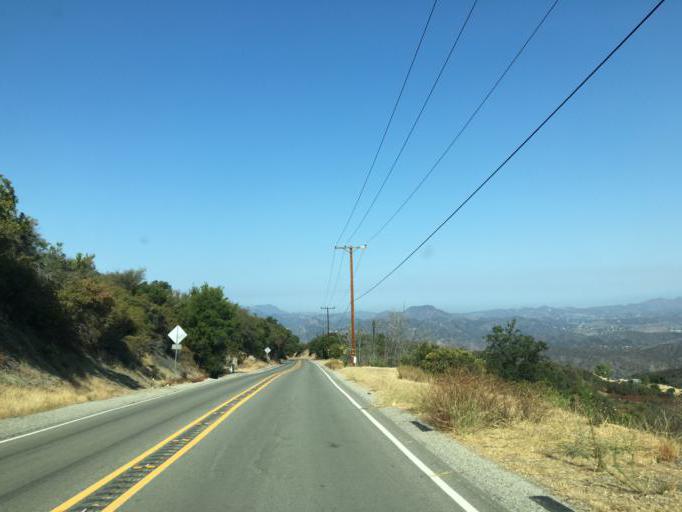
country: US
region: California
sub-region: Los Angeles County
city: Las Flores
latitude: 34.0861
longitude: -118.6606
